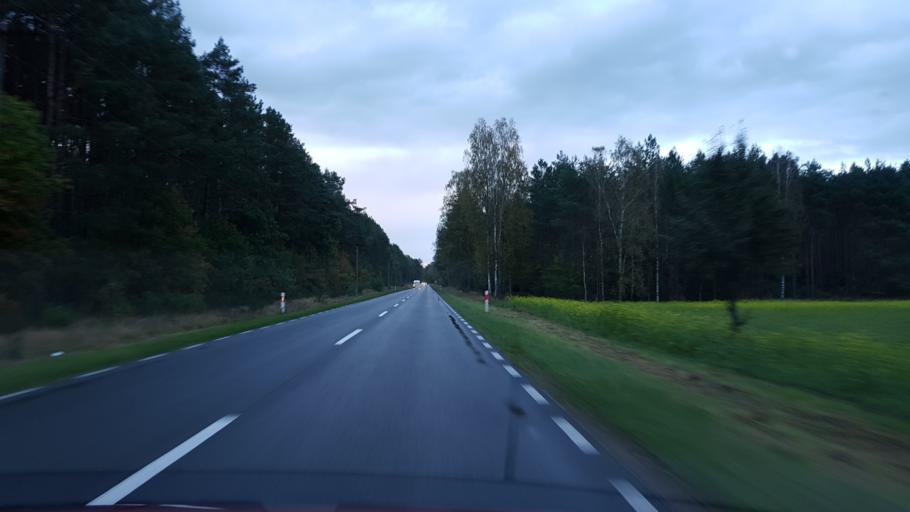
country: PL
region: Greater Poland Voivodeship
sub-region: Powiat zlotowski
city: Tarnowka
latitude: 53.2456
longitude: 16.8906
